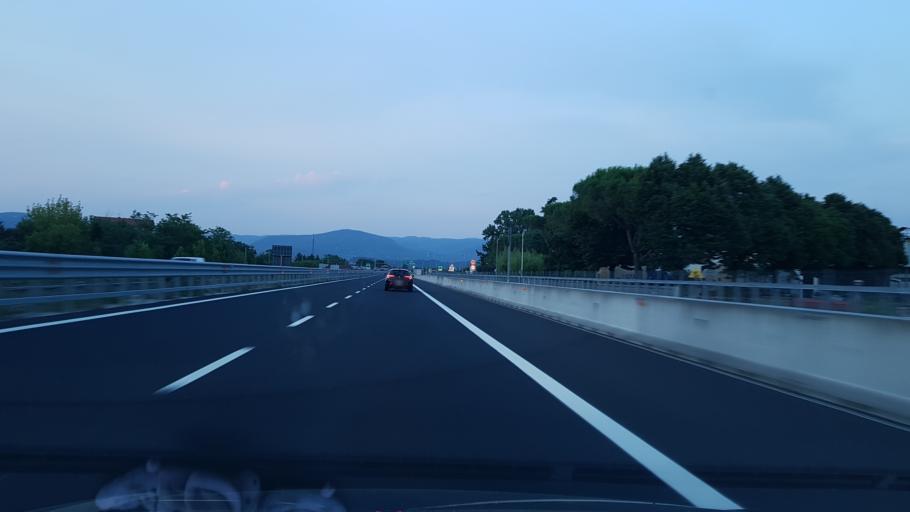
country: SI
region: Miren-Kostanjevica
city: Miren
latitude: 45.9130
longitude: 13.5990
